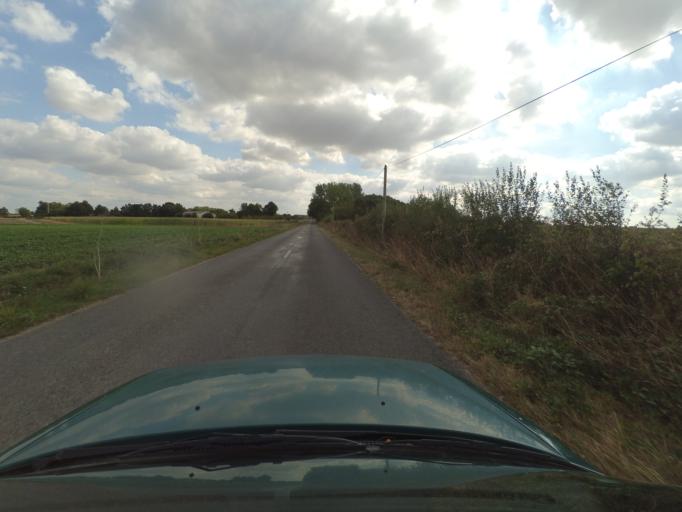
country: FR
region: Pays de la Loire
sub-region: Departement de la Loire-Atlantique
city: La Planche
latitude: 47.0013
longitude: -1.4552
